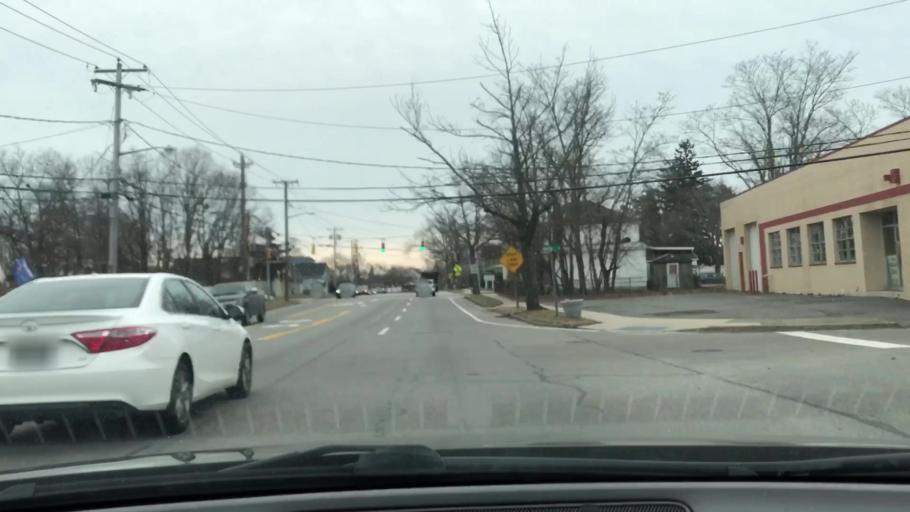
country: US
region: New York
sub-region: Suffolk County
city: Patchogue
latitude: 40.7708
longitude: -73.0274
